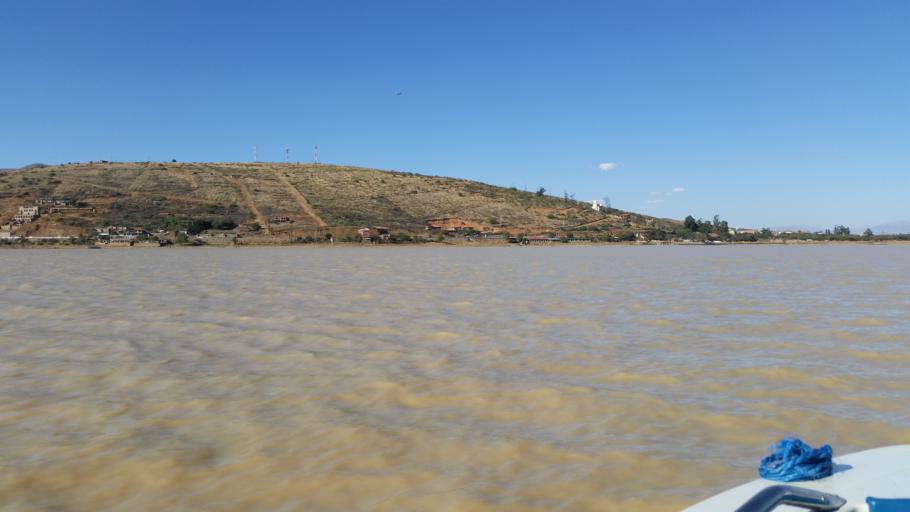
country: BO
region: Cochabamba
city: Tarata
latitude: -17.5353
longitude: -66.0897
